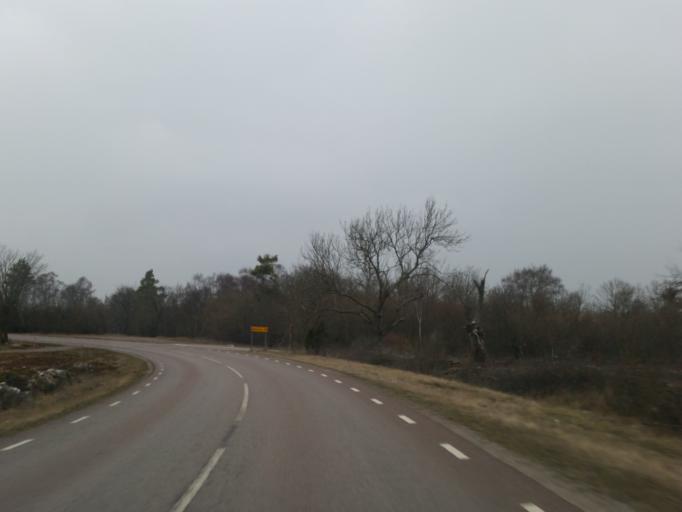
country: SE
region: Kalmar
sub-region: Morbylanga Kommun
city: Sodra Sandby
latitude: 56.6491
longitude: 16.5781
